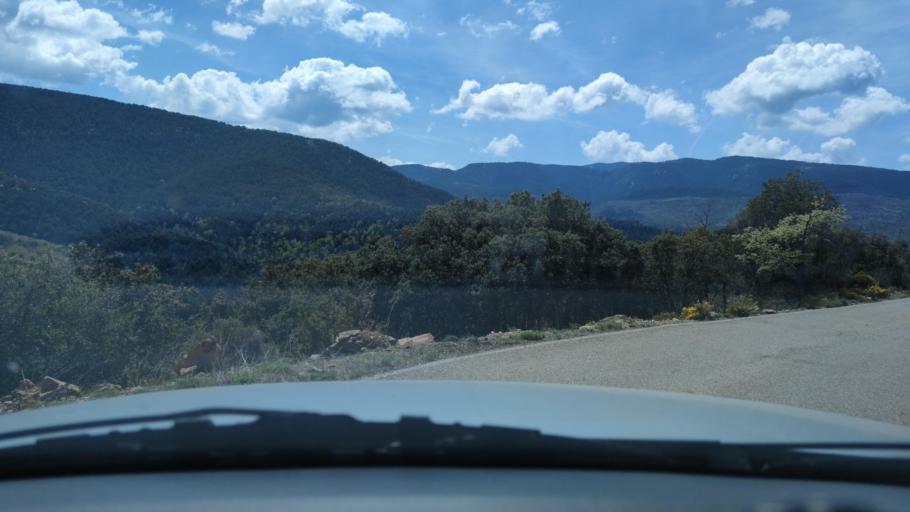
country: ES
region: Catalonia
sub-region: Provincia de Lleida
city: Sort
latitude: 42.3149
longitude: 1.1349
